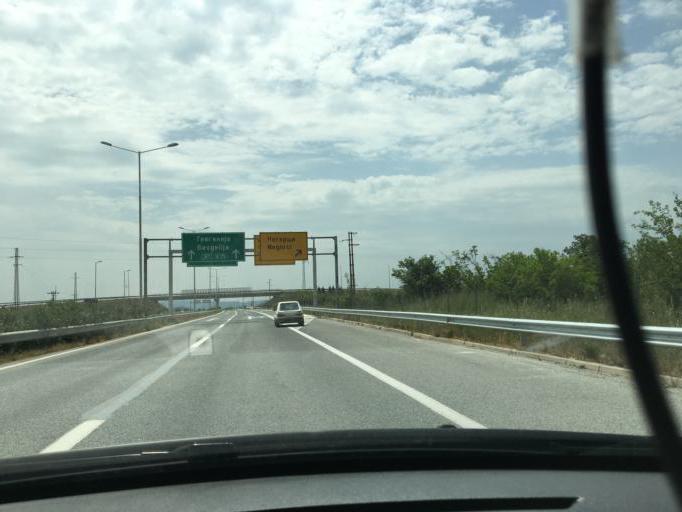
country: MK
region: Gevgelija
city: Gevgelija
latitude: 41.2059
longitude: 22.4954
